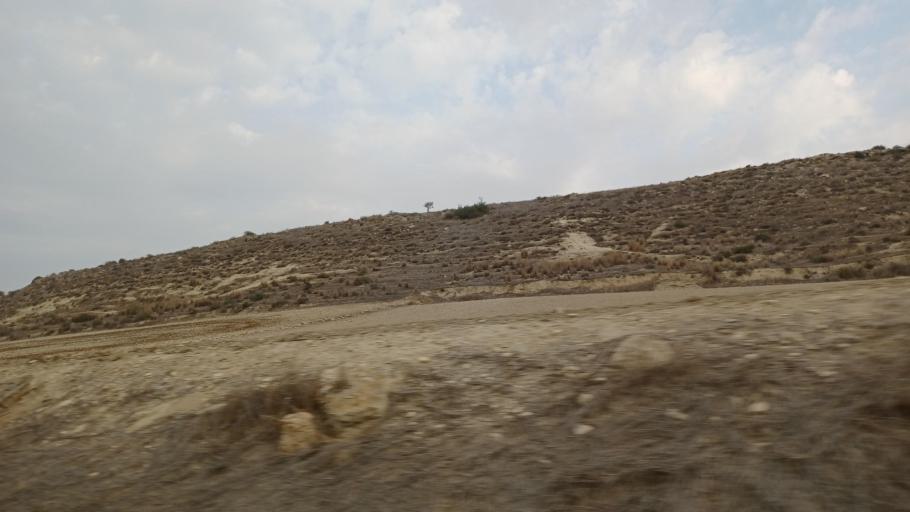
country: CY
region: Larnaka
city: Athienou
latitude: 35.0379
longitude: 33.5599
